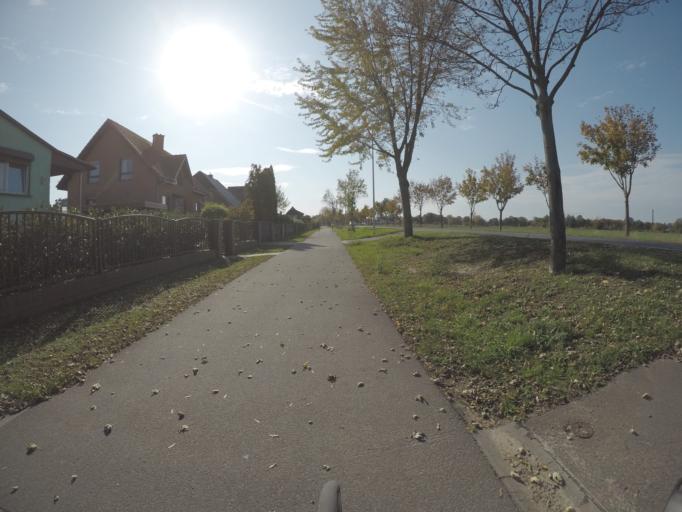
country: DE
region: Brandenburg
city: Velten
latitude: 52.6897
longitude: 13.1959
